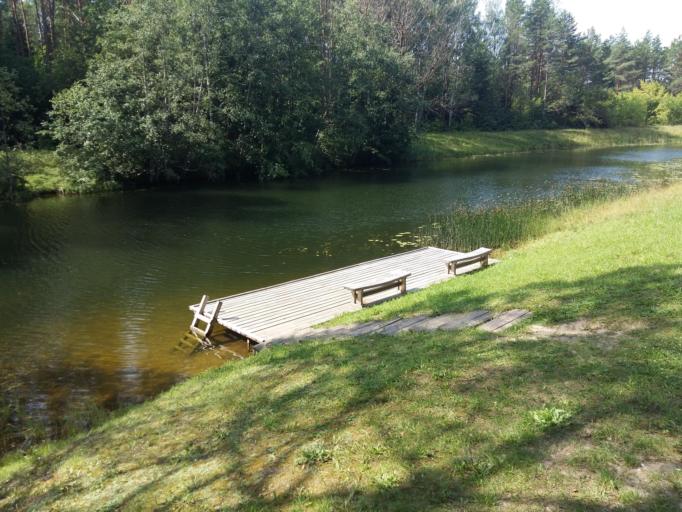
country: LT
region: Utenos apskritis
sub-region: Utena
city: Utena
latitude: 55.6549
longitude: 25.8857
